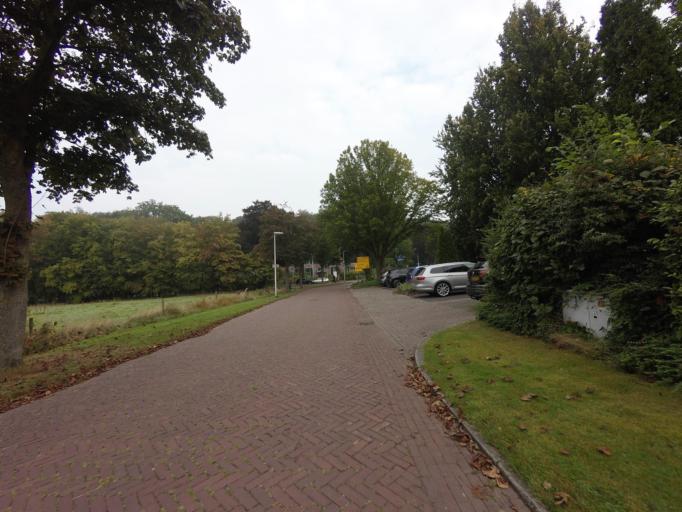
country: NL
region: Overijssel
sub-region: Gemeente Deventer
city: Schalkhaar
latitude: 52.2664
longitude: 6.1845
